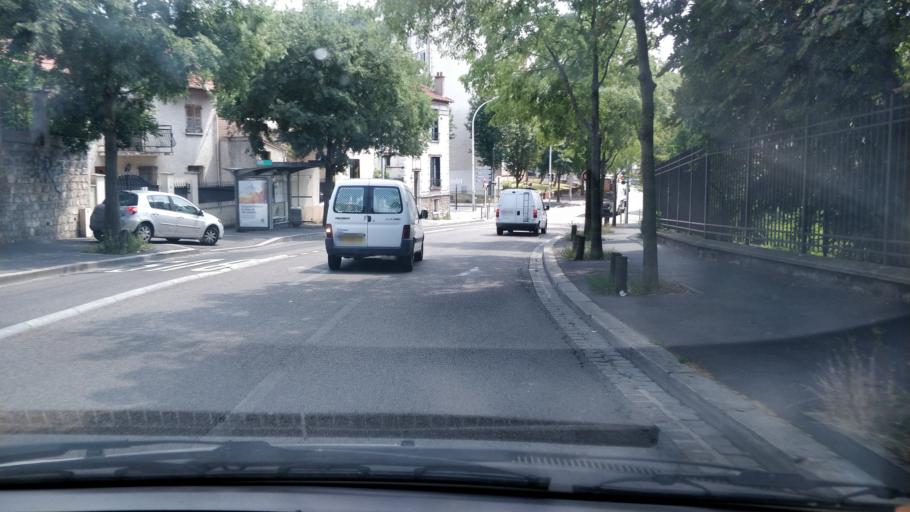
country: FR
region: Ile-de-France
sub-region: Departement de Seine-Saint-Denis
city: Les Lilas
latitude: 48.8760
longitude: 2.4237
